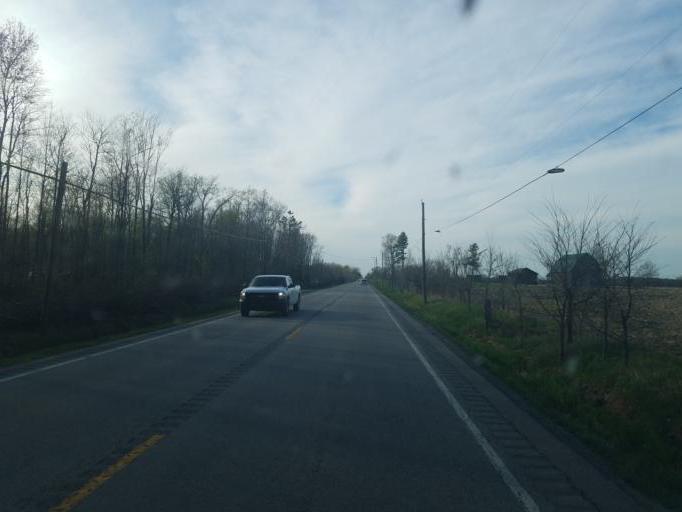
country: US
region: Ohio
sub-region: Huron County
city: Norwalk
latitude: 41.1600
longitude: -82.5452
